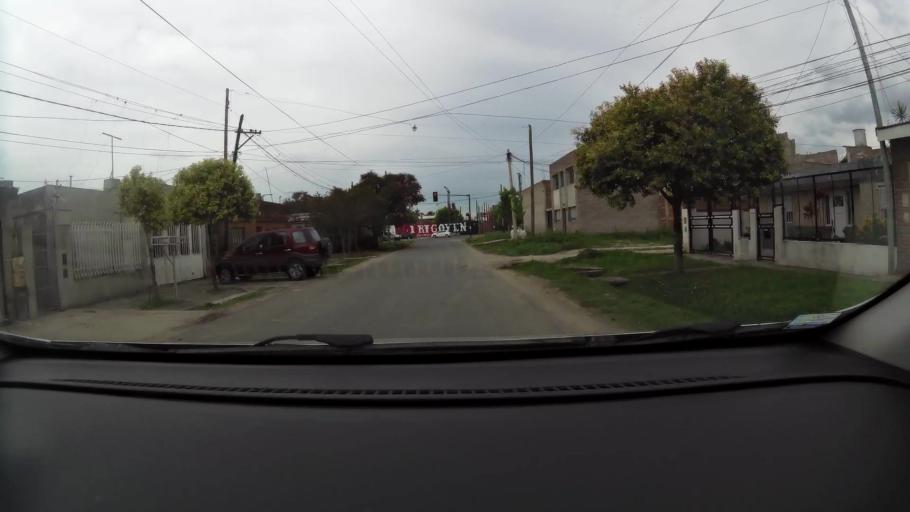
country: AR
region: Santa Fe
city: Gobernador Galvez
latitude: -33.0150
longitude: -60.6528
